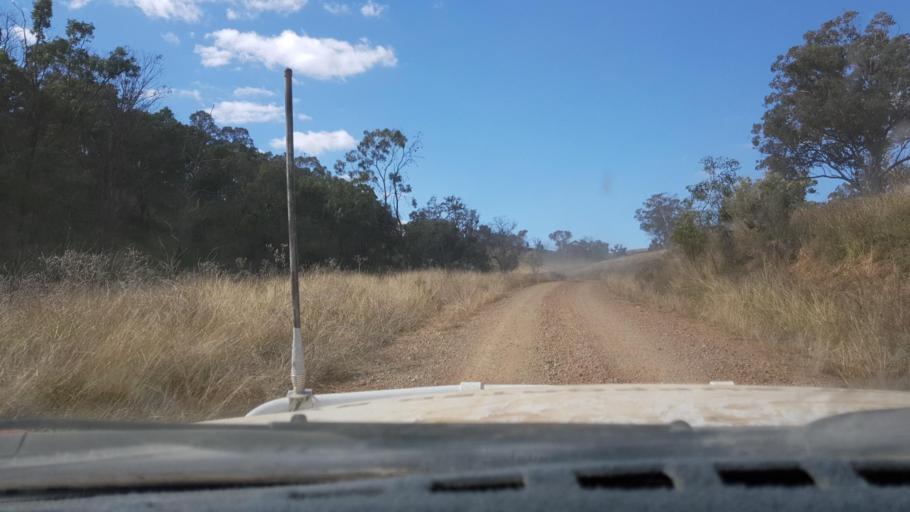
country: AU
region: New South Wales
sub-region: Tamworth Municipality
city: Manilla
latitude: -30.4379
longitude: 150.8431
